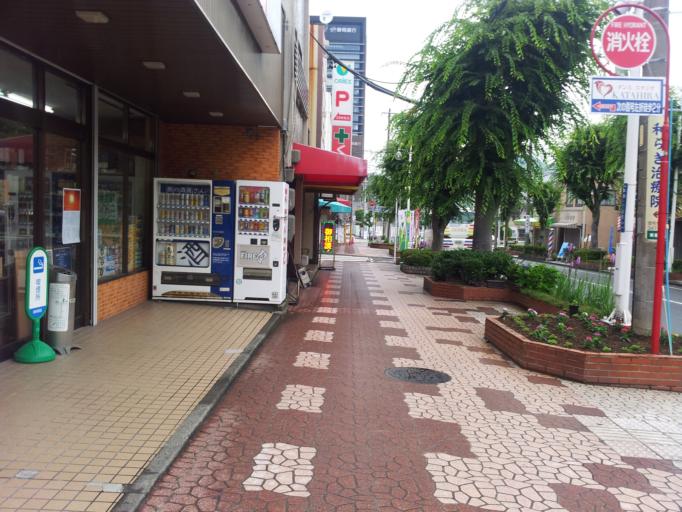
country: JP
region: Shizuoka
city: Shizuoka-shi
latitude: 35.0019
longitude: 138.4429
